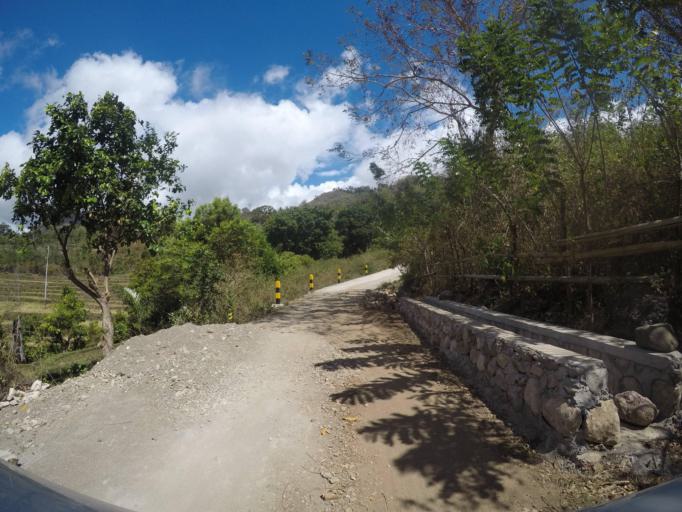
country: TL
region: Lautem
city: Lospalos
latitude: -8.5380
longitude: 126.8010
